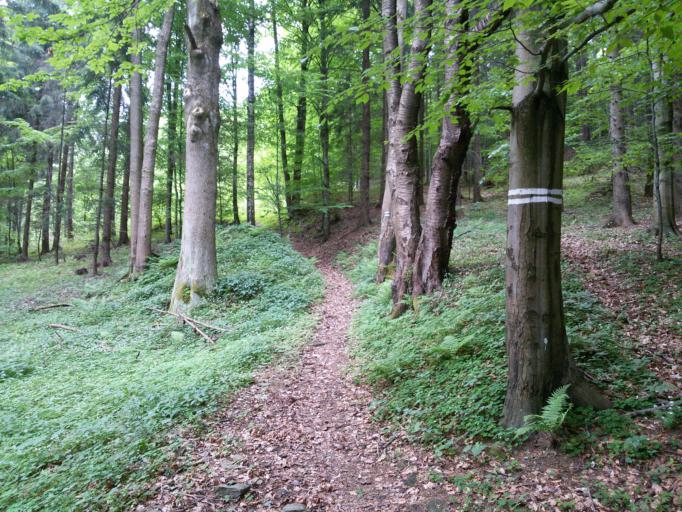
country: CZ
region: Olomoucky
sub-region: Okres Sumperk
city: Loucna nad Desnou
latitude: 50.1036
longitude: 17.1108
